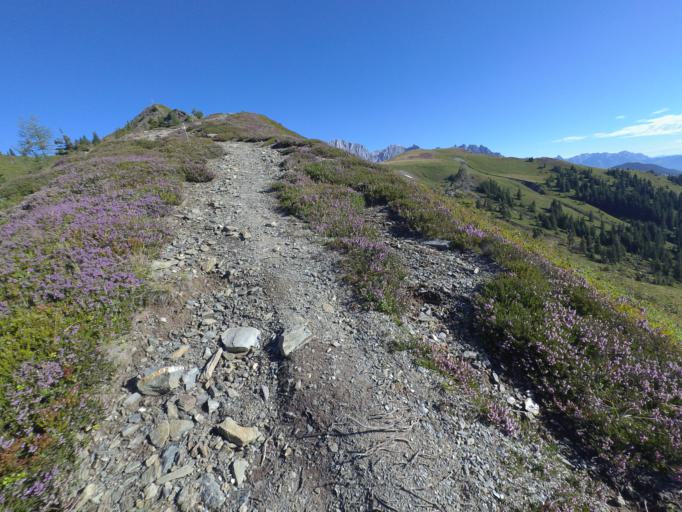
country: AT
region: Salzburg
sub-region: Politischer Bezirk Sankt Johann im Pongau
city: Goldegg
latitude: 47.3634
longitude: 13.0705
